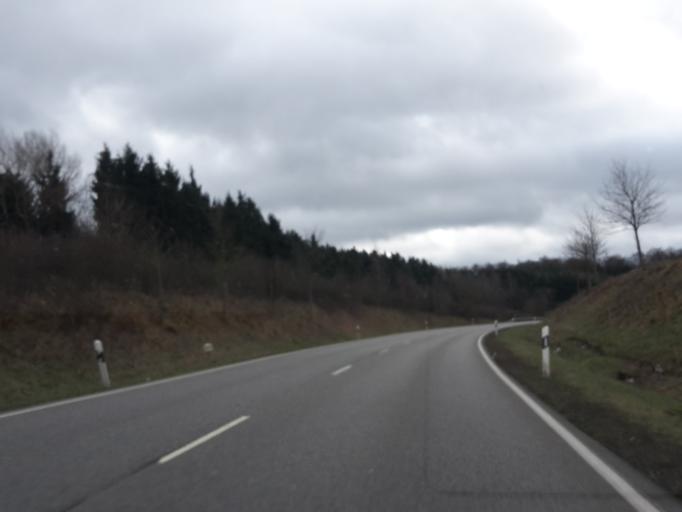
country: DE
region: Hesse
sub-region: Regierungsbezirk Darmstadt
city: Idstein
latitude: 50.1692
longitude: 8.2225
